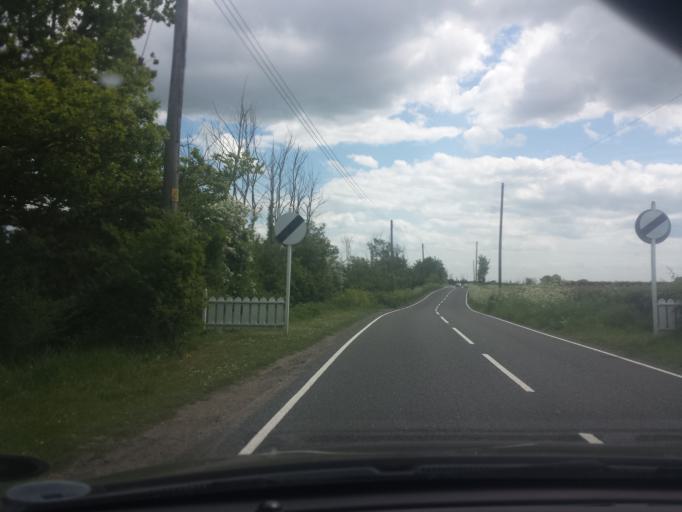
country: GB
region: England
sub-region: Essex
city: Little Clacton
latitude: 51.8391
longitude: 1.1542
